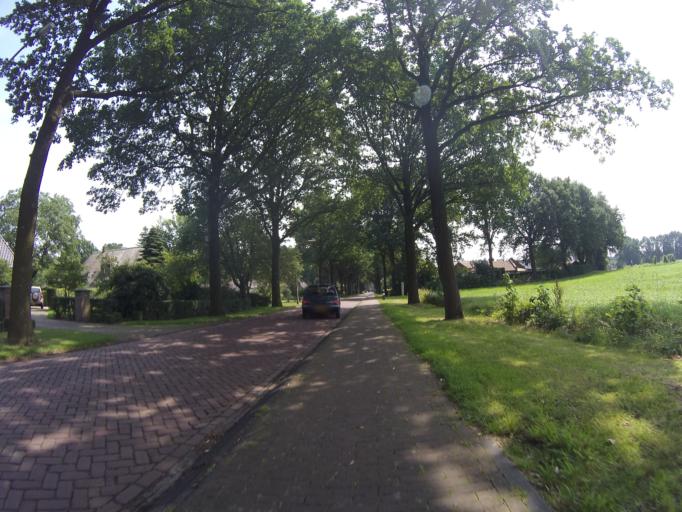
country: NL
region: Drenthe
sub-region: Gemeente Coevorden
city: Sleen
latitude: 52.7897
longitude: 6.7132
